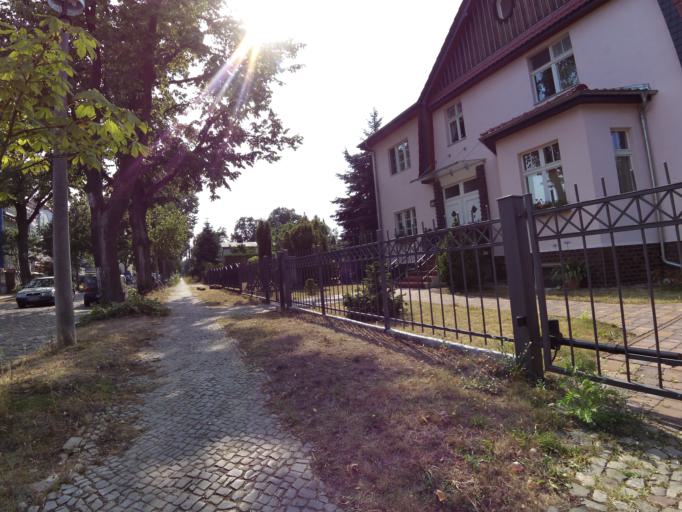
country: DE
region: Berlin
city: Grunau
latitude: 52.4132
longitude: 13.5583
